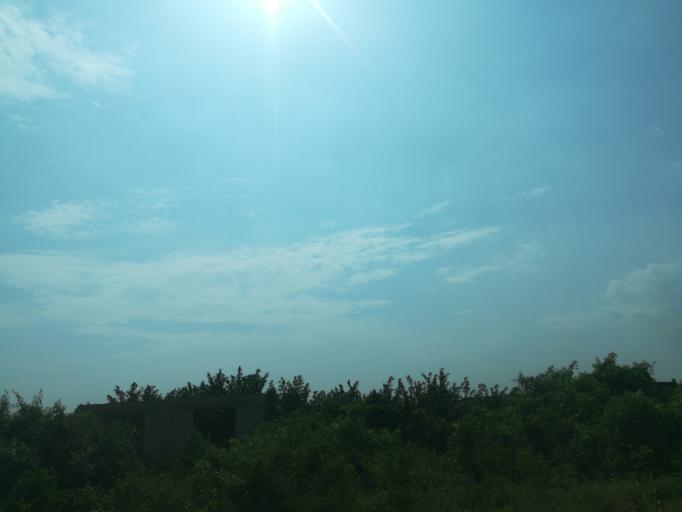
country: NG
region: Lagos
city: Ikorodu
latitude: 6.6362
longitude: 3.6700
